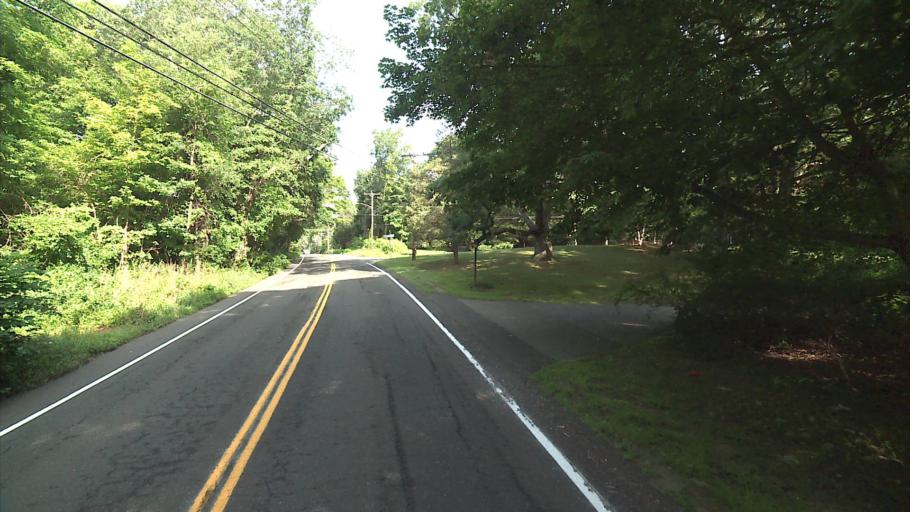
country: US
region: Connecticut
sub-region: New Haven County
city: Woodbridge
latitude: 41.3568
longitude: -73.0390
